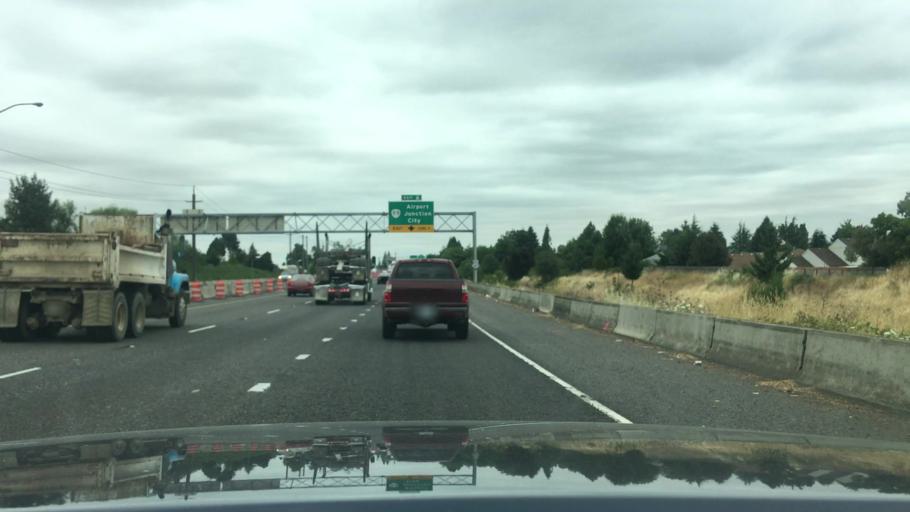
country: US
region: Oregon
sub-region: Lane County
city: Eugene
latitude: 44.0883
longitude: -123.1713
